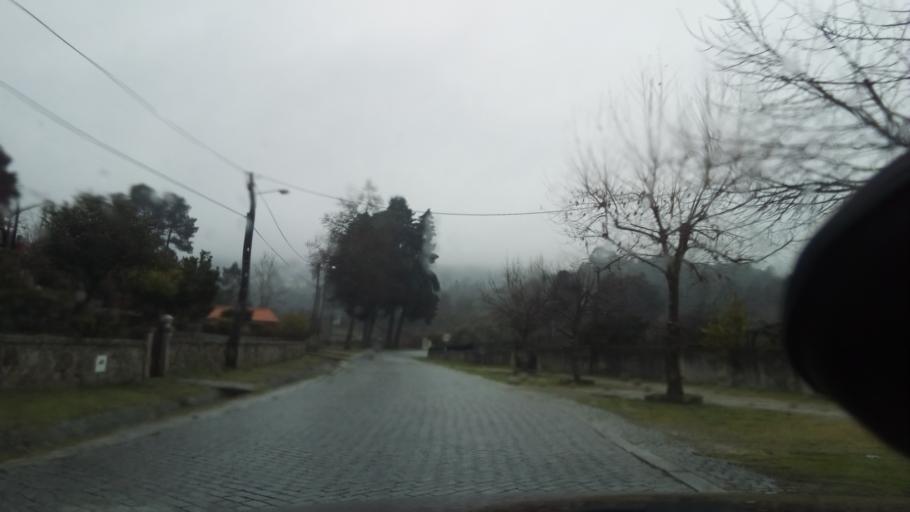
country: PT
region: Viseu
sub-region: Mangualde
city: Mangualde
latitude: 40.6088
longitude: -7.6861
